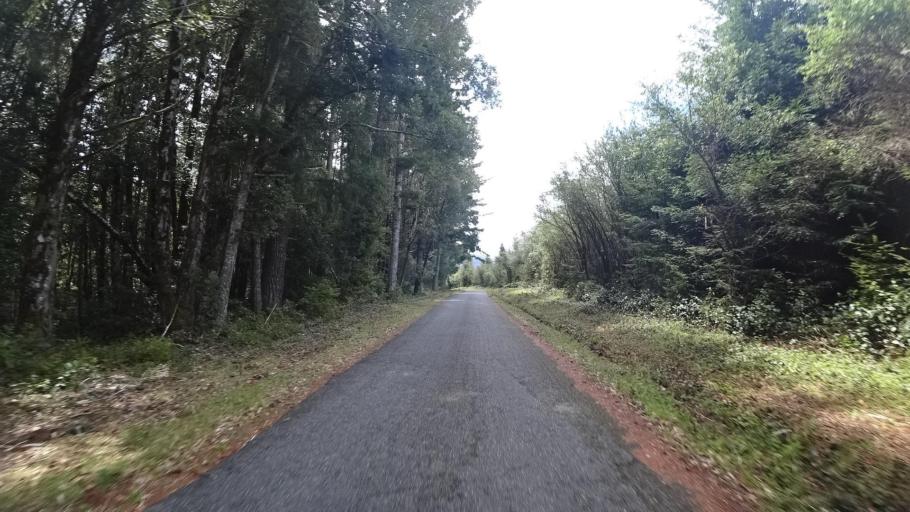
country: US
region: California
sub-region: Humboldt County
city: Blue Lake
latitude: 40.7793
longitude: -123.9626
